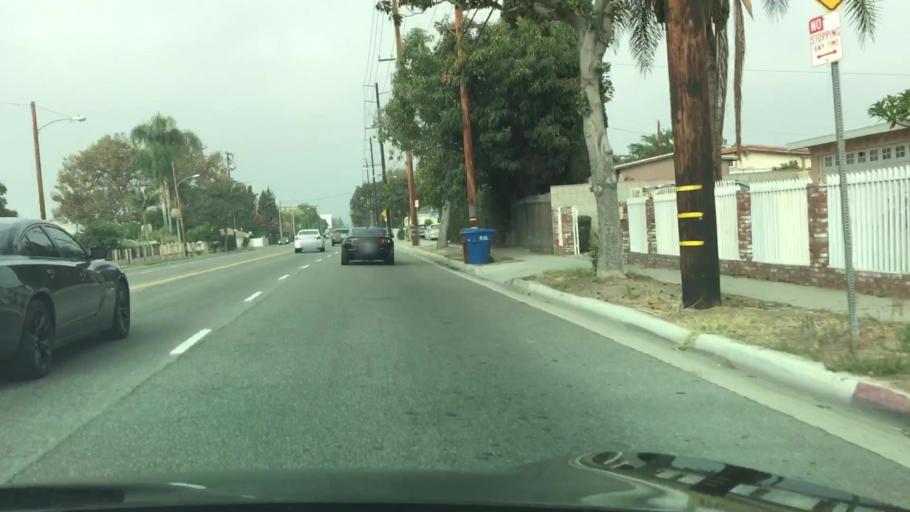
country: US
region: California
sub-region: Los Angeles County
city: West Puente Valley
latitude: 34.0512
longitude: -117.9827
